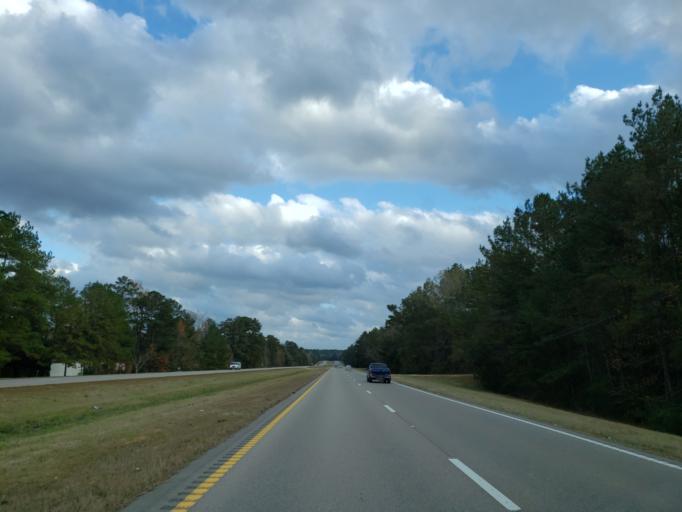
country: US
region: Mississippi
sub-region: Perry County
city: New Augusta
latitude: 31.2202
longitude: -89.1760
